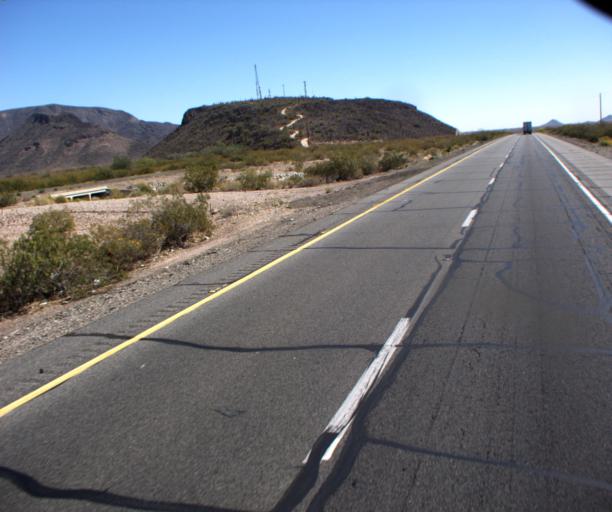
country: US
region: Arizona
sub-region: La Paz County
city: Salome
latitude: 33.5300
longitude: -113.1226
